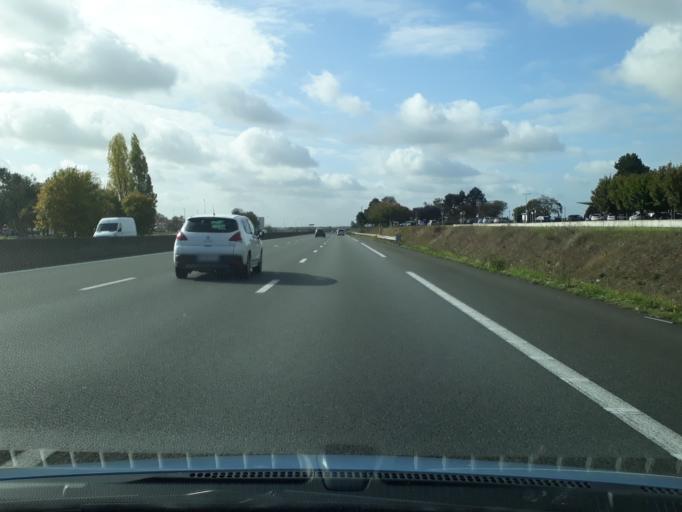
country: FR
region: Centre
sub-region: Departement du Loir-et-Cher
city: La Chaussee-Saint-Victor
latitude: 47.6659
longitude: 1.3885
